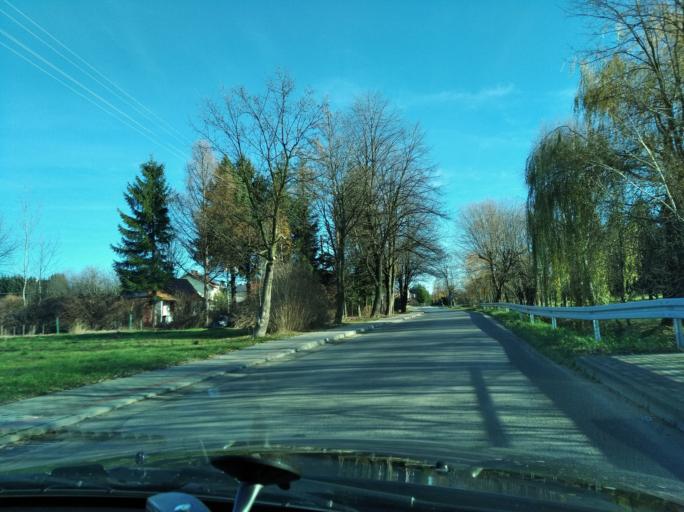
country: PL
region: Subcarpathian Voivodeship
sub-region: Powiat rzeszowski
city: Lutoryz
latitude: 49.9791
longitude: 21.9017
